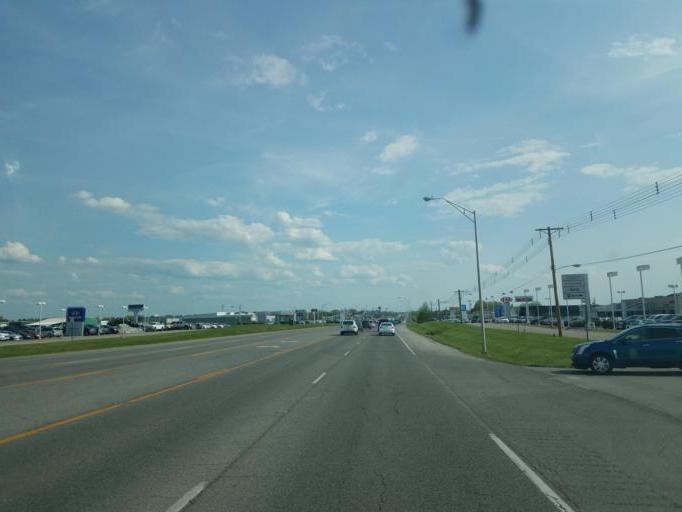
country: US
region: Kentucky
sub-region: Warren County
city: Bowling Green
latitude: 36.9580
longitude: -86.4286
